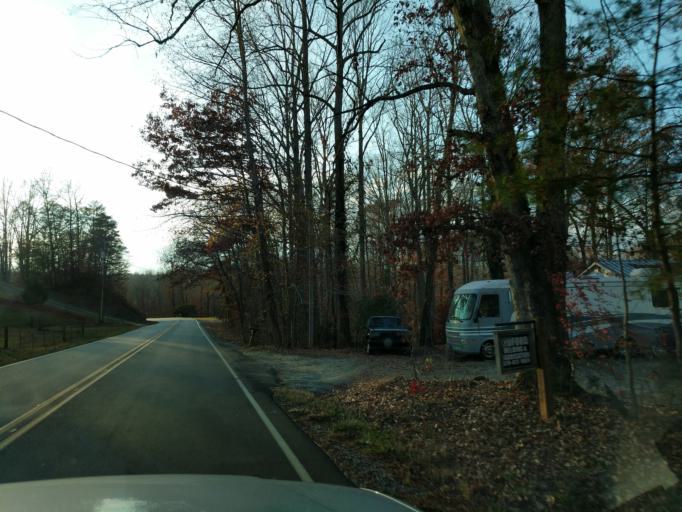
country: US
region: North Carolina
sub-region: Rutherford County
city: Rutherfordton
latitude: 35.2736
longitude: -82.0346
